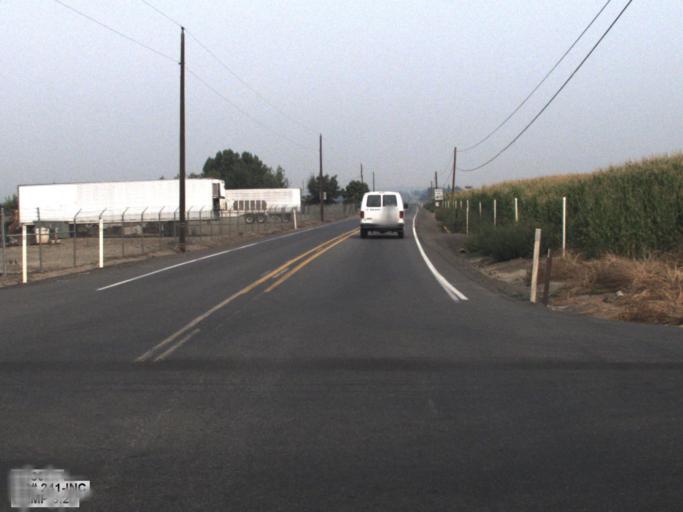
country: US
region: Washington
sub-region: Yakima County
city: Sunnyside
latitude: 46.3171
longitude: -119.9791
